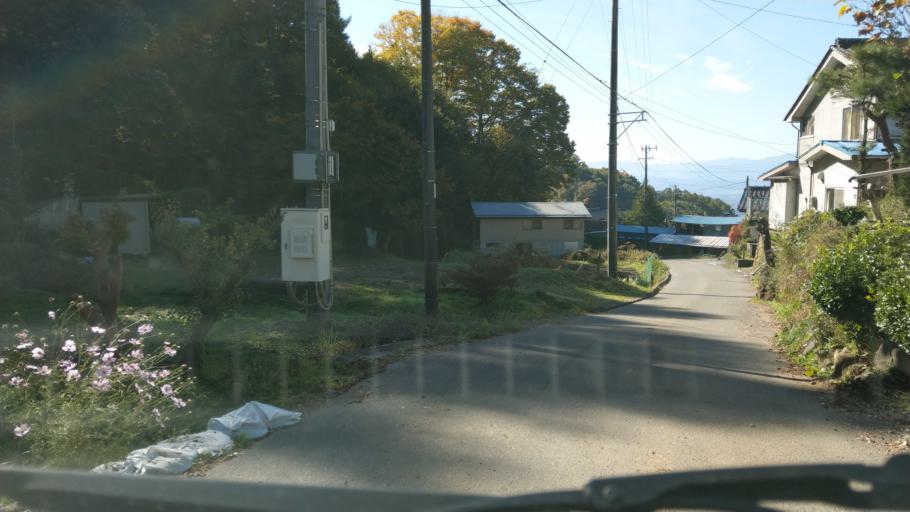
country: JP
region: Nagano
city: Komoro
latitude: 36.3666
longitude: 138.4048
